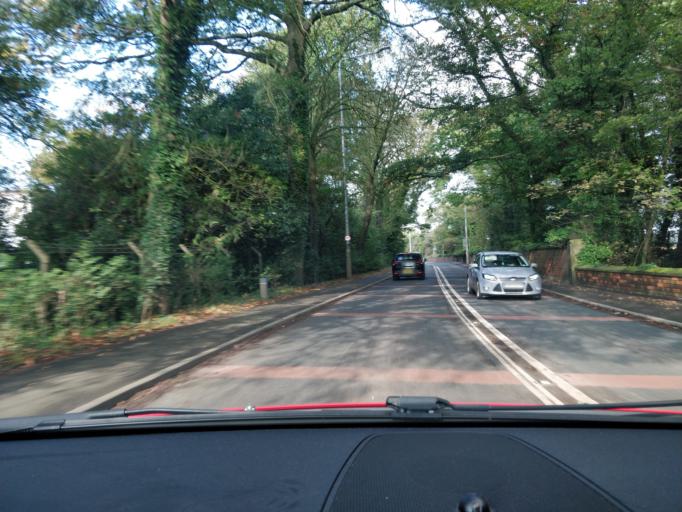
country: GB
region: England
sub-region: Lancashire
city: Ormskirk
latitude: 53.6057
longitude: -2.9338
